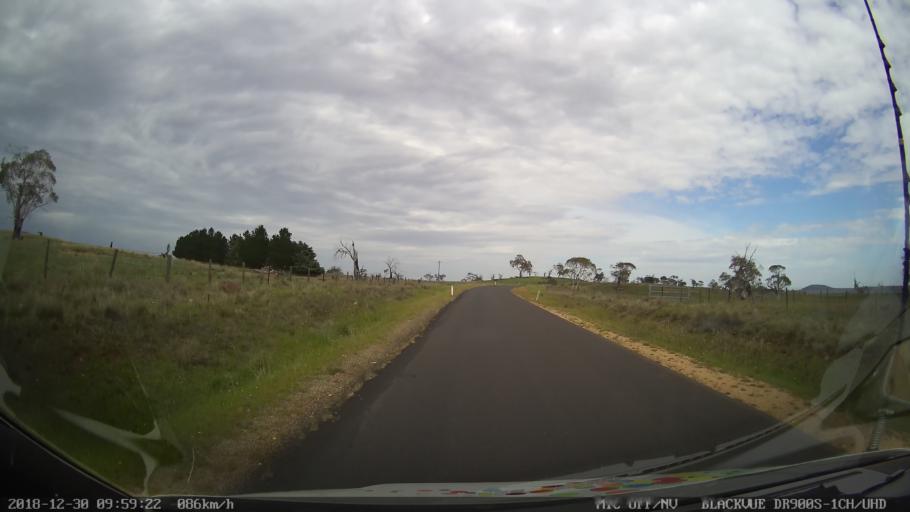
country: AU
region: New South Wales
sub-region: Cooma-Monaro
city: Cooma
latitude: -36.5228
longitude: 149.2114
